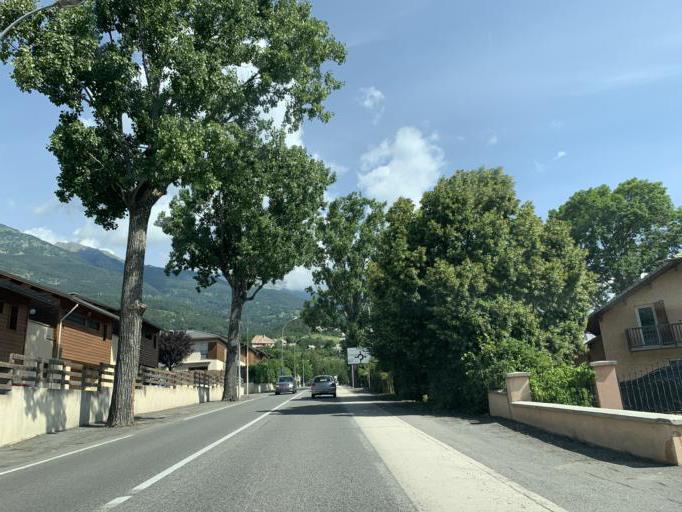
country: FR
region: Provence-Alpes-Cote d'Azur
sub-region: Departement des Hautes-Alpes
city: Embrun
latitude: 44.5542
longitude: 6.4836
